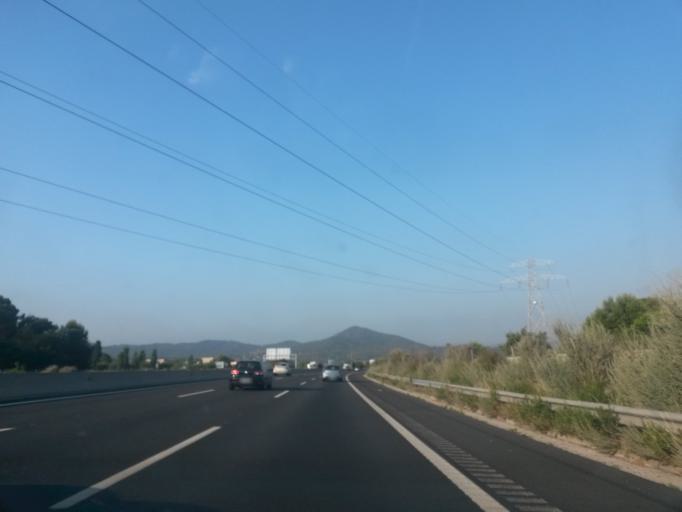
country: ES
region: Catalonia
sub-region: Provincia de Barcelona
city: Rubi
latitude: 41.4808
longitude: 2.0465
